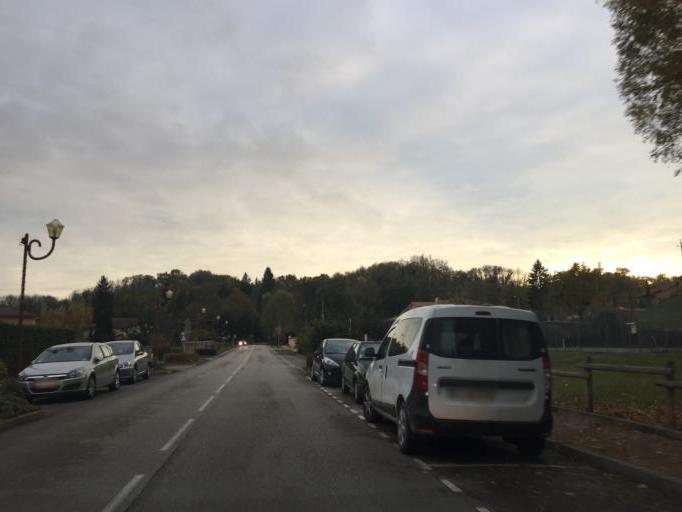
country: FR
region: Rhone-Alpes
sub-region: Departement de l'Ain
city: Chatillon-la-Palud
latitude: 45.9441
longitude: 5.2440
